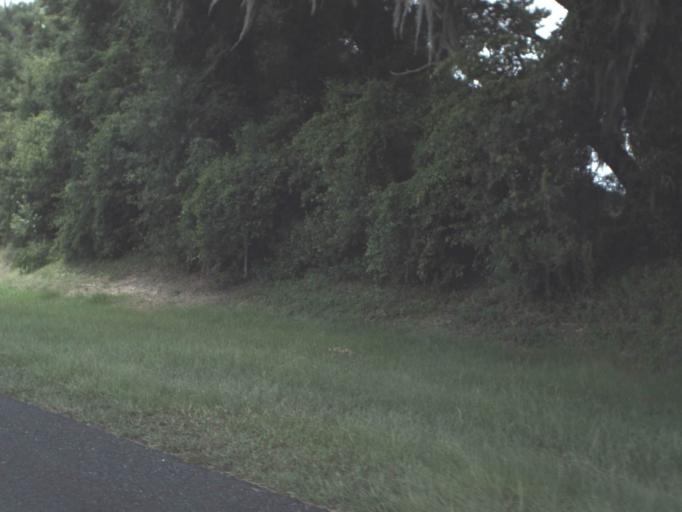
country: US
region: Florida
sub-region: Levy County
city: Williston
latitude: 29.3804
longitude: -82.4225
